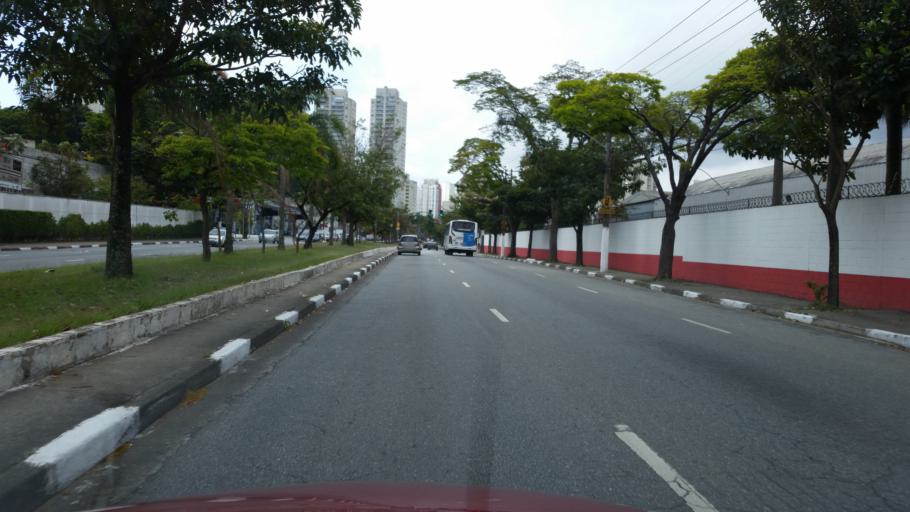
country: BR
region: Sao Paulo
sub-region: Diadema
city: Diadema
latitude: -23.6706
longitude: -46.6962
